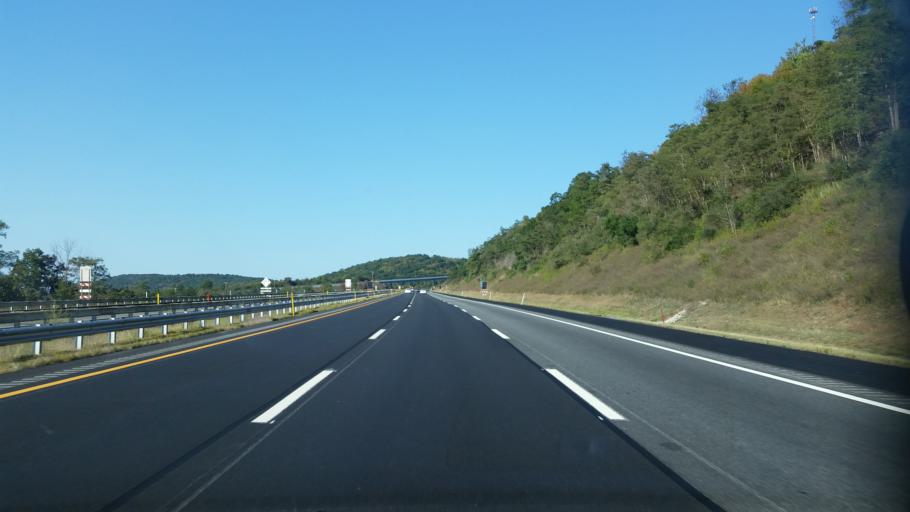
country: US
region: Pennsylvania
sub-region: Bedford County
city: Earlston
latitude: 40.0052
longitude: -78.2124
